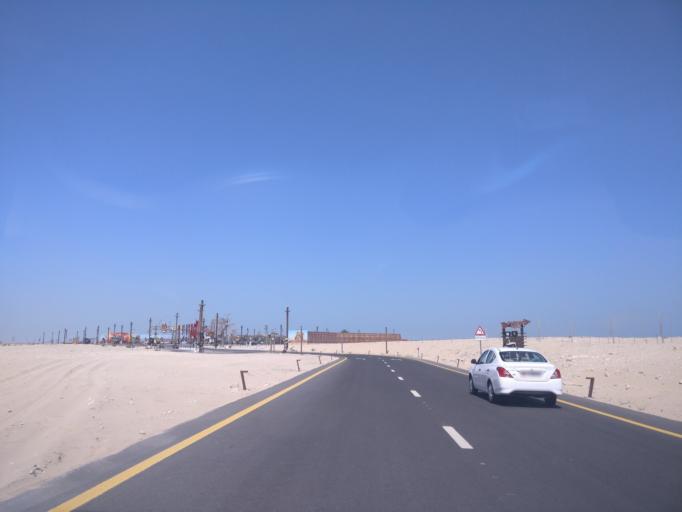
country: AE
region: Dubai
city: Dubai
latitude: 24.9139
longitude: 54.9645
